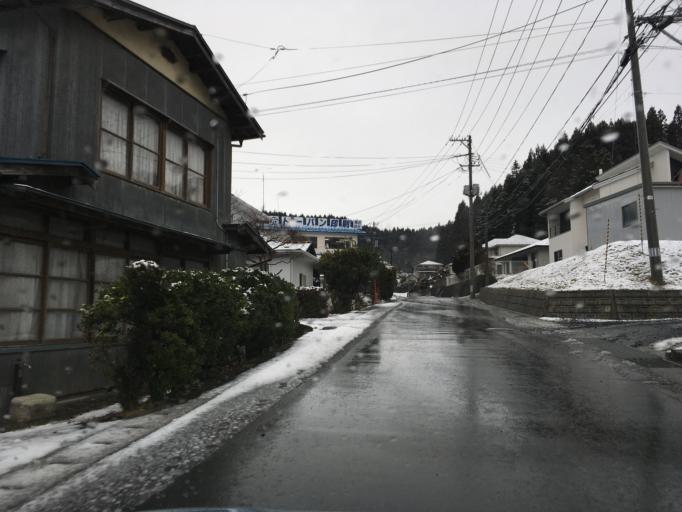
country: JP
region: Iwate
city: Ichinoseki
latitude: 38.9151
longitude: 141.3267
